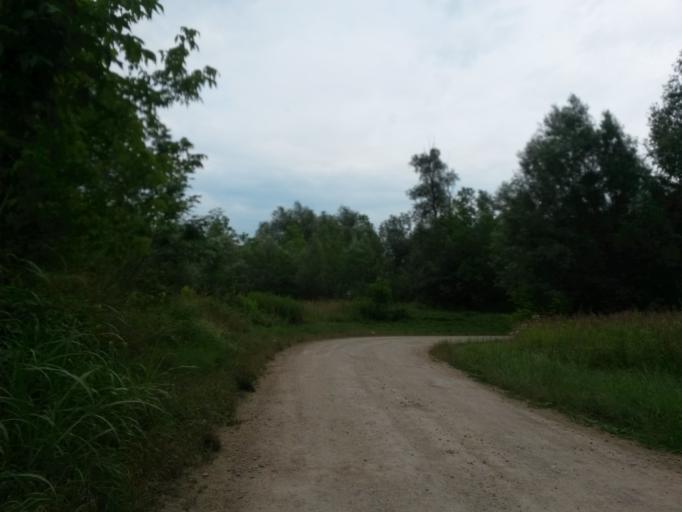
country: HR
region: Osjecko-Baranjska
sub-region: Grad Osijek
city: Bilje
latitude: 45.5926
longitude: 18.7395
